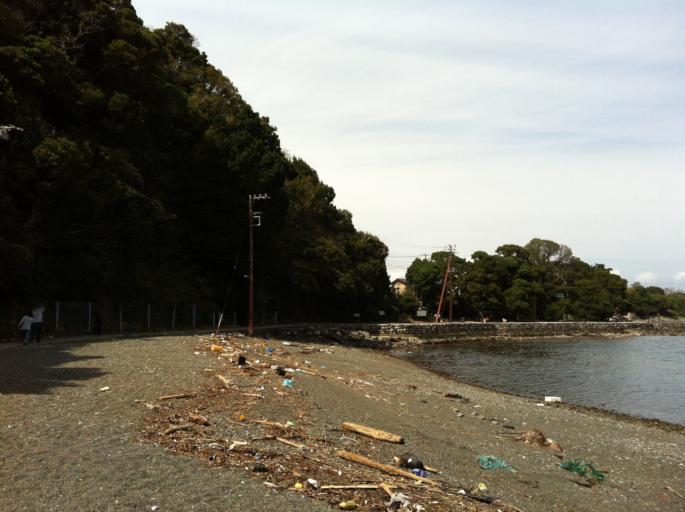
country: JP
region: Shizuoka
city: Heda
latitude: 35.0256
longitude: 138.7859
